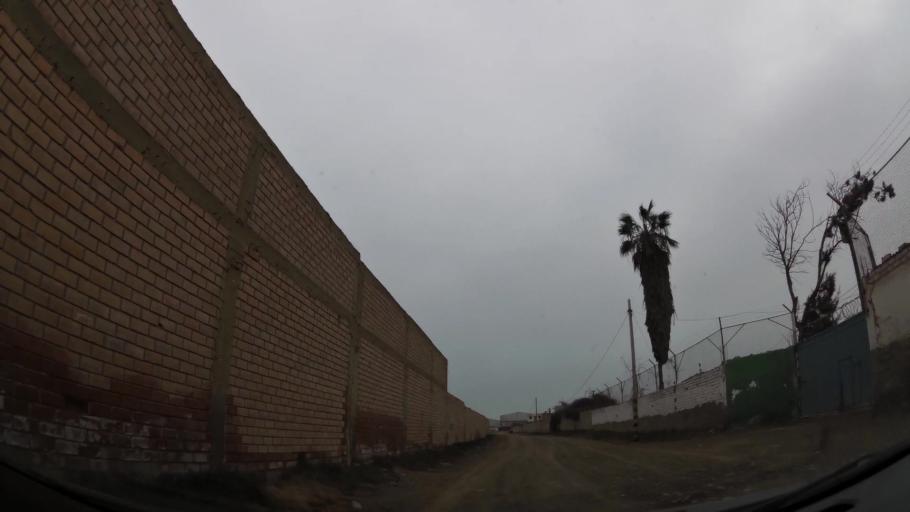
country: PE
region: Lima
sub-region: Lima
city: Surco
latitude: -12.2039
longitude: -76.9855
